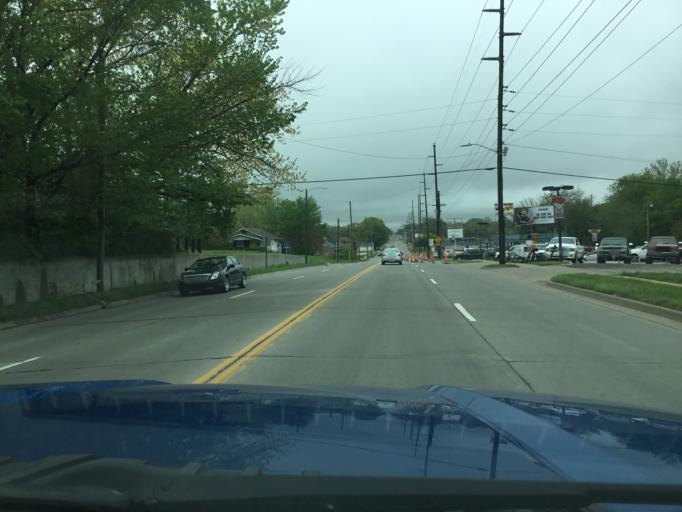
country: US
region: Kansas
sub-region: Shawnee County
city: Topeka
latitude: 39.0297
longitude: -95.6940
